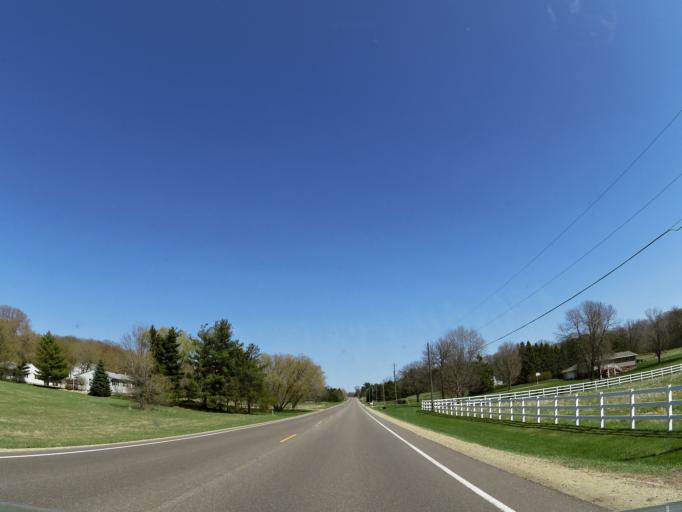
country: US
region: Wisconsin
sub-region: Saint Croix County
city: Hudson
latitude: 44.9599
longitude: -92.6751
